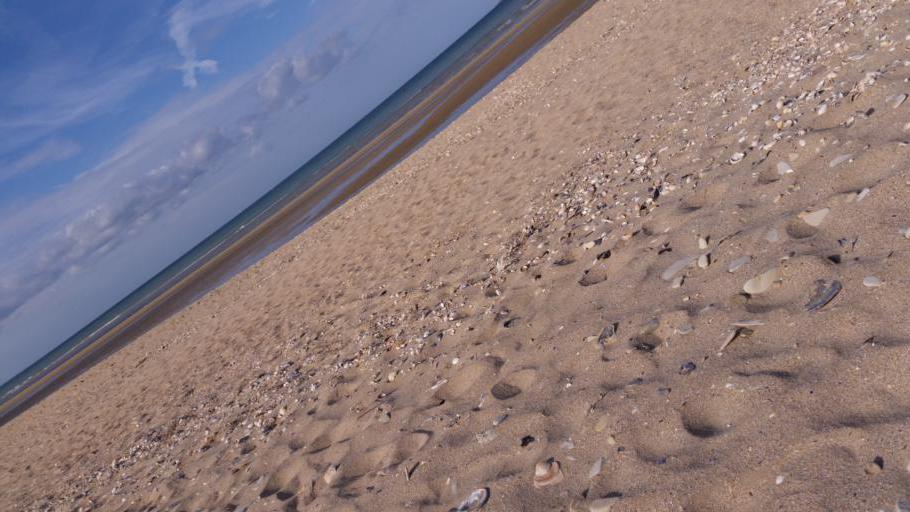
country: FR
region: Lower Normandy
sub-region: Departement de la Manche
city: Sainte-Mere-Eglise
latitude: 49.4458
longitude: -1.2101
